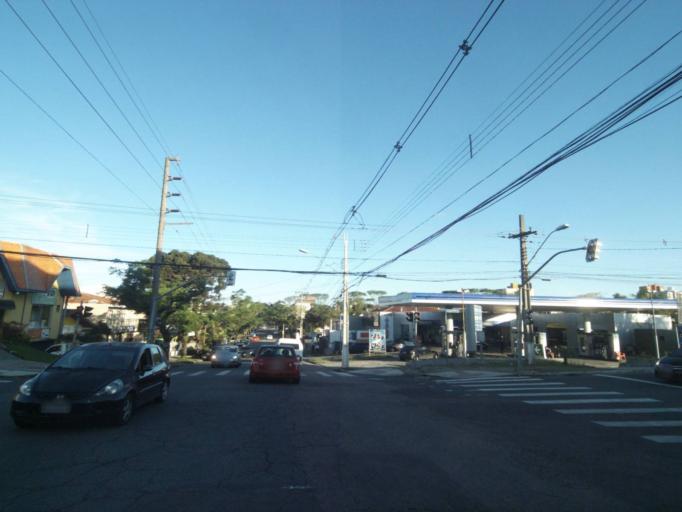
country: BR
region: Parana
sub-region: Curitiba
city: Curitiba
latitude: -25.3884
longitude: -49.2437
